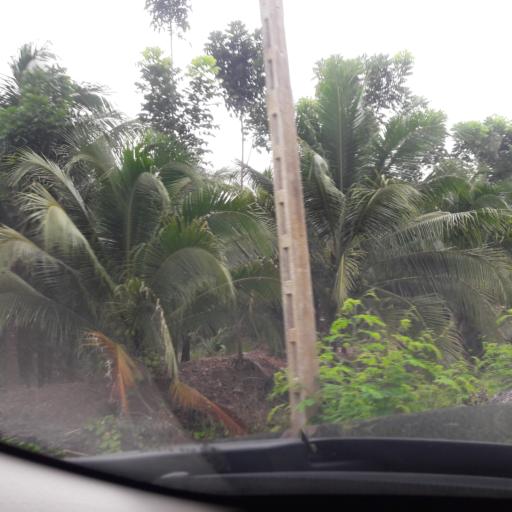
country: TH
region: Ratchaburi
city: Damnoen Saduak
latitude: 13.5841
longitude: 99.9403
